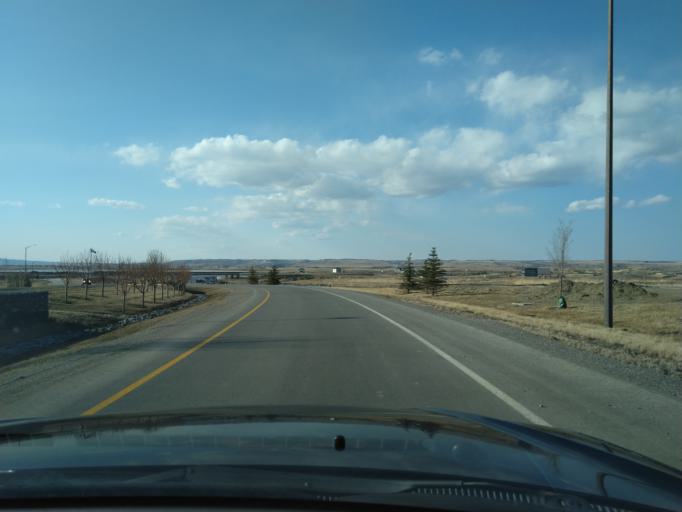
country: CA
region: Alberta
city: Cochrane
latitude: 51.1108
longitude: -114.3905
